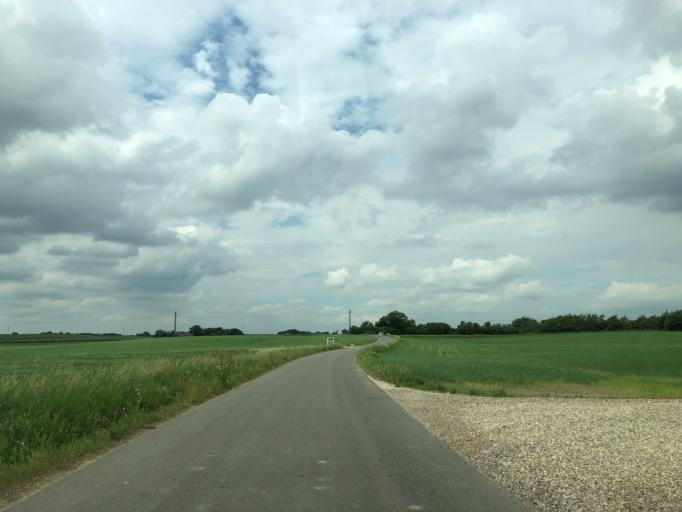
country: DK
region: Central Jutland
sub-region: Struer Kommune
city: Struer
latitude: 56.4648
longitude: 8.5836
